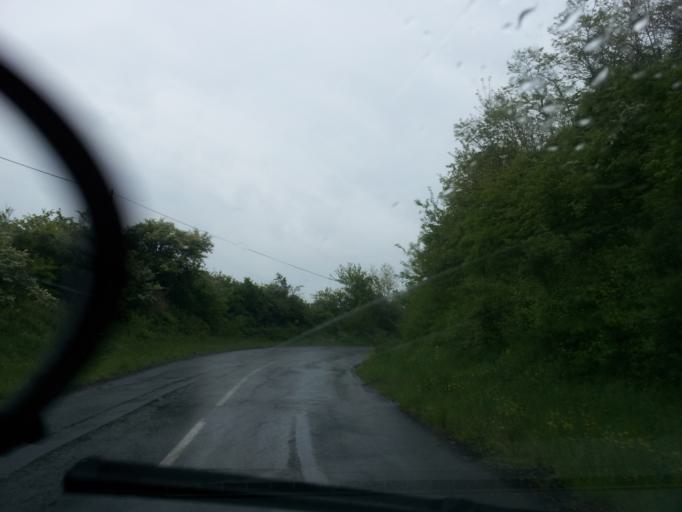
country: HU
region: Tolna
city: Szekszard
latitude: 46.2893
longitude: 18.6653
